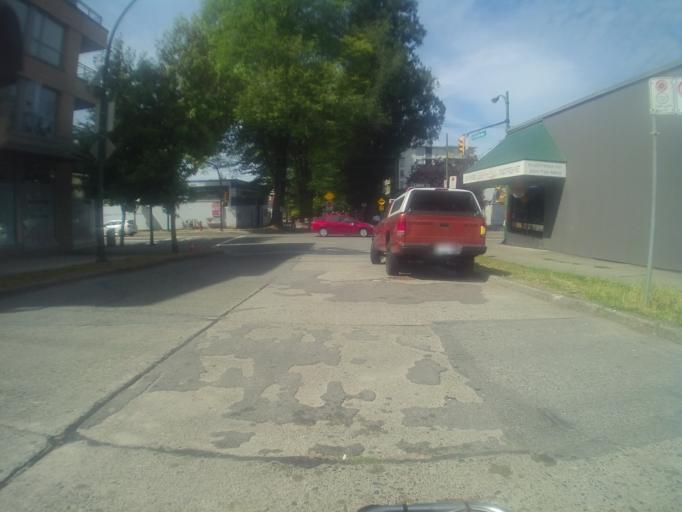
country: CA
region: British Columbia
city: West End
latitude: 49.2629
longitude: -123.1526
